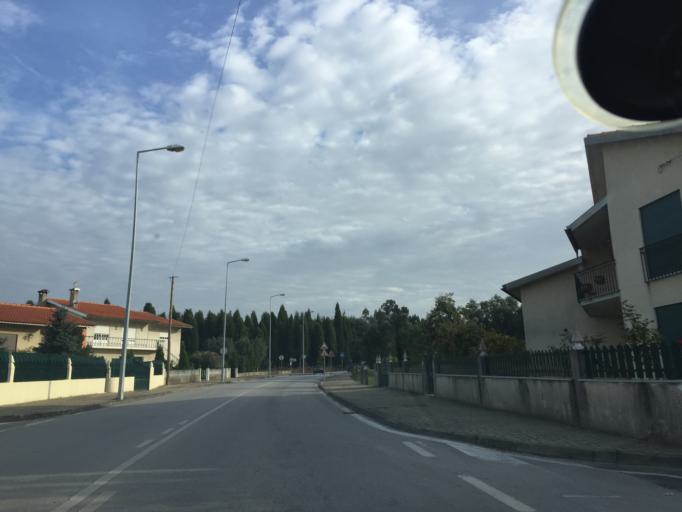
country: PT
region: Aveiro
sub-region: Anadia
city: Arcos
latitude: 40.4528
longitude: -8.4342
